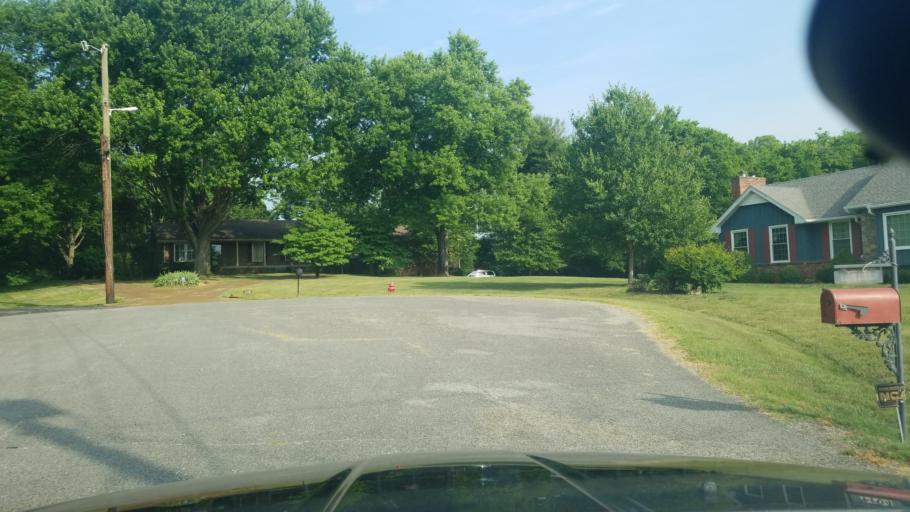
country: US
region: Tennessee
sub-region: Davidson County
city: Goodlettsville
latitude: 36.2777
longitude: -86.7604
